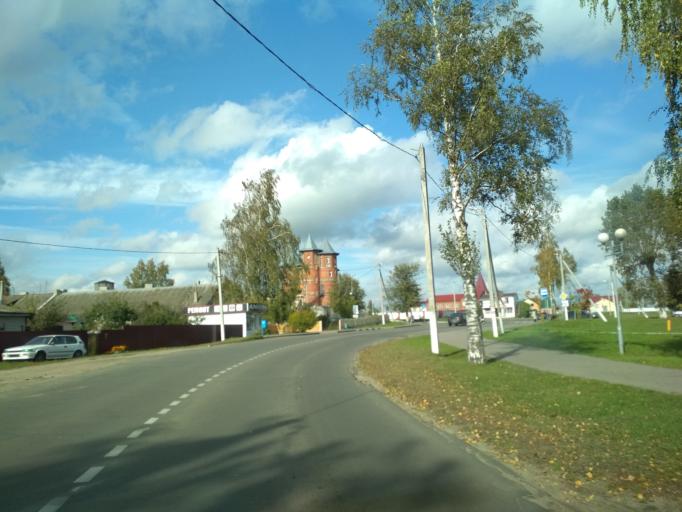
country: BY
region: Minsk
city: Mar''ina Horka
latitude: 53.5062
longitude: 28.1546
